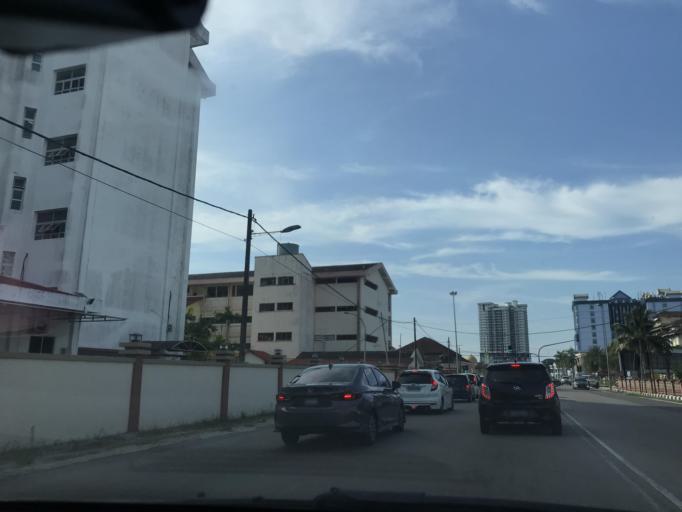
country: MY
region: Kelantan
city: Kota Bharu
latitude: 6.1237
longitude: 102.2471
